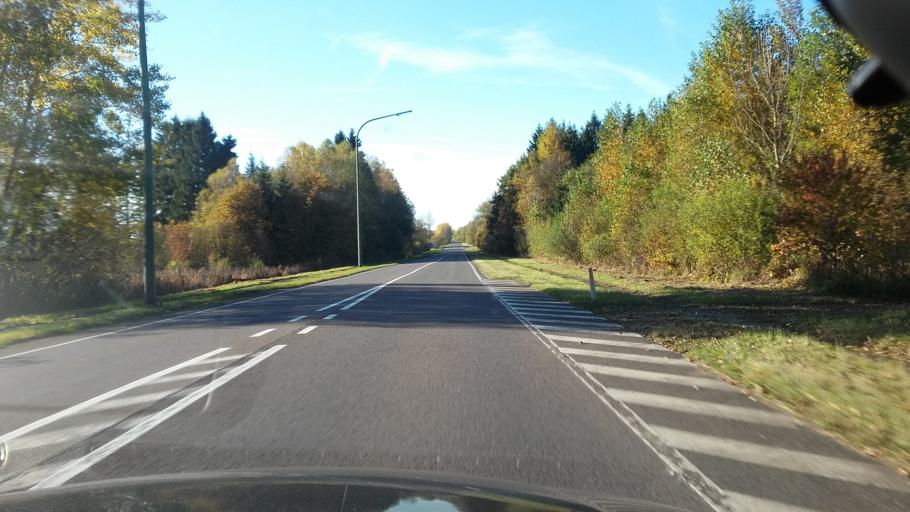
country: BE
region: Wallonia
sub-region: Province du Luxembourg
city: Etalle
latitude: 49.6728
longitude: 5.6394
